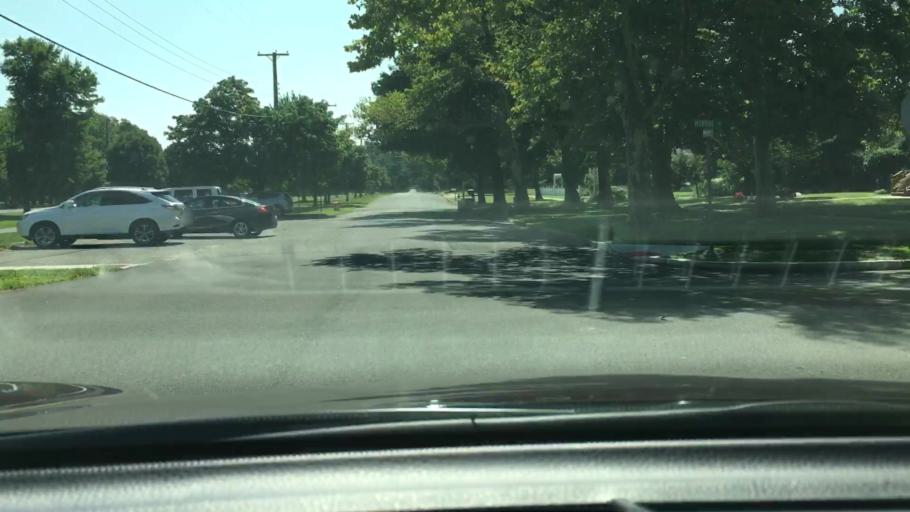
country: US
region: New Jersey
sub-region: Cape May County
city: Woodbine
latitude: 39.2391
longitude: -74.8115
